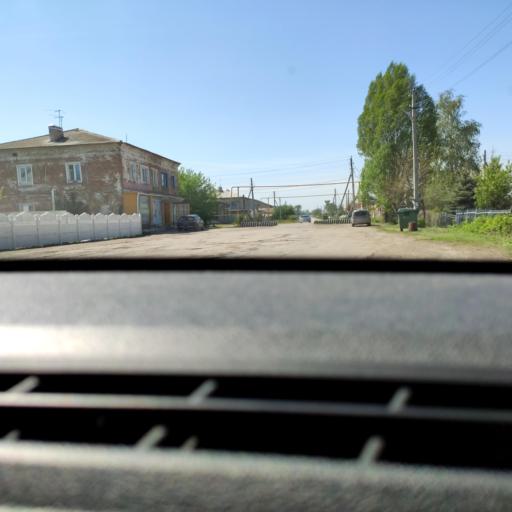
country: RU
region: Samara
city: Tol'yatti
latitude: 53.6774
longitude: 49.4266
